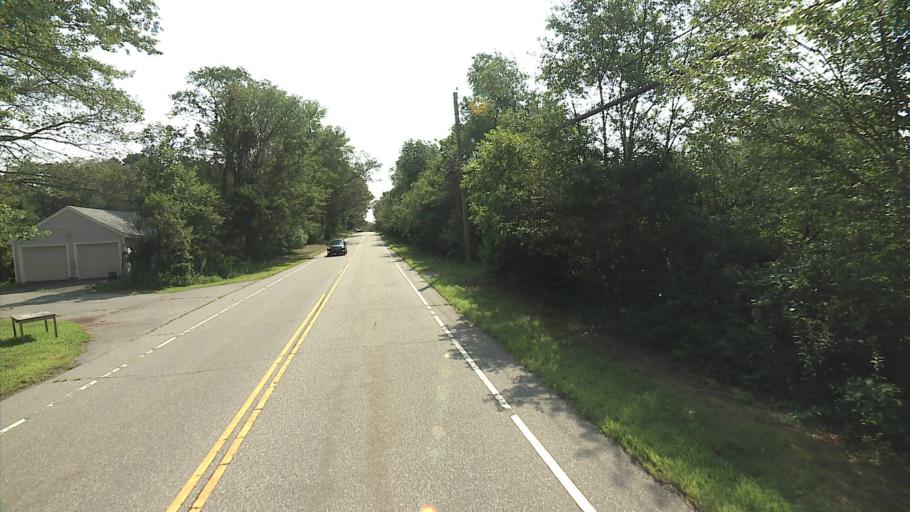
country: US
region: Connecticut
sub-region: New London County
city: Colchester
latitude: 41.5719
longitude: -72.2371
